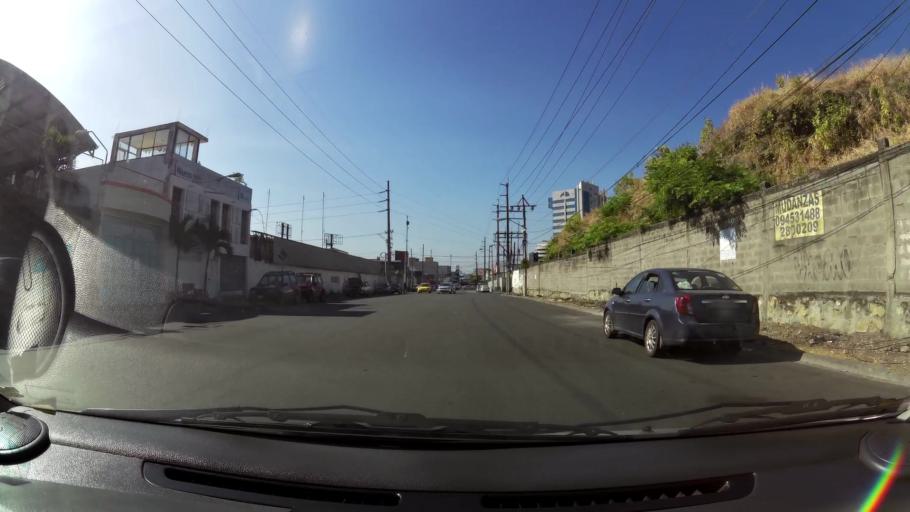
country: EC
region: Guayas
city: Eloy Alfaro
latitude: -2.1558
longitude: -79.8980
